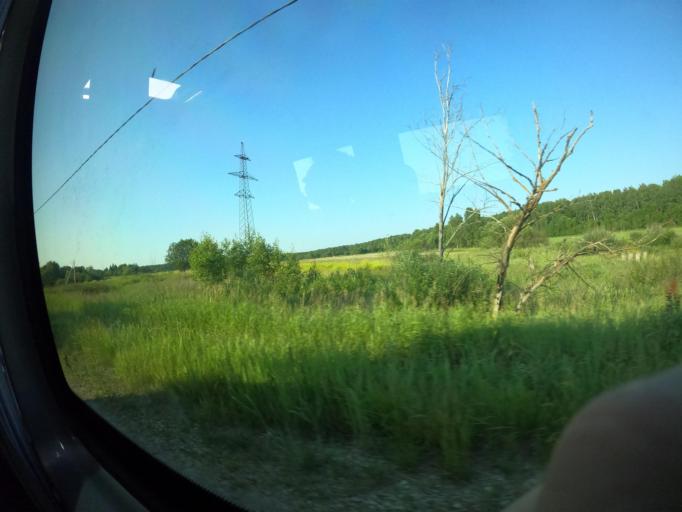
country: RU
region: Moskovskaya
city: Obolensk
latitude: 54.9307
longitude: 37.2524
